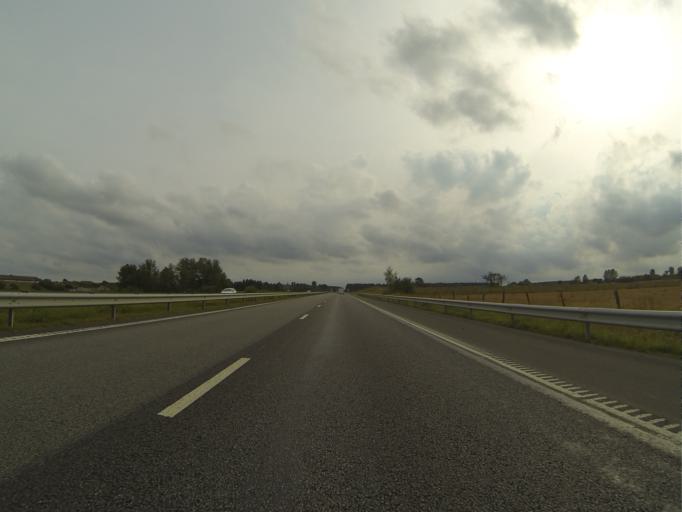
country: SE
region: Skane
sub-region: Kristianstads Kommun
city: Norra Asum
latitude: 55.9909
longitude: 14.0930
